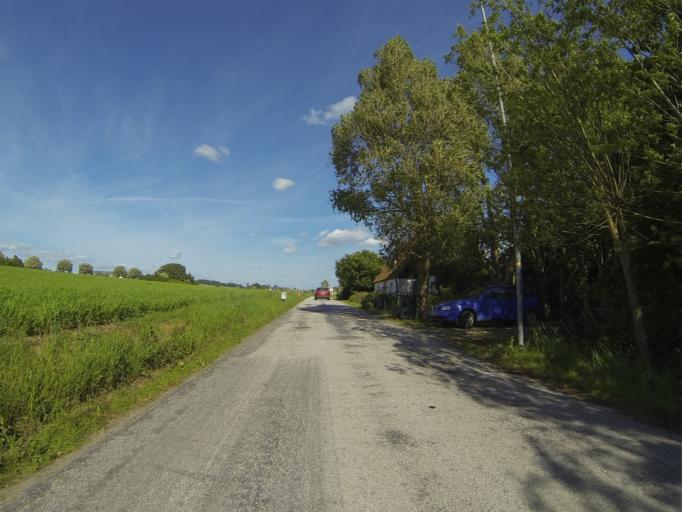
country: SE
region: Skane
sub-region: Lunds Kommun
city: Lund
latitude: 55.6870
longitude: 13.2513
